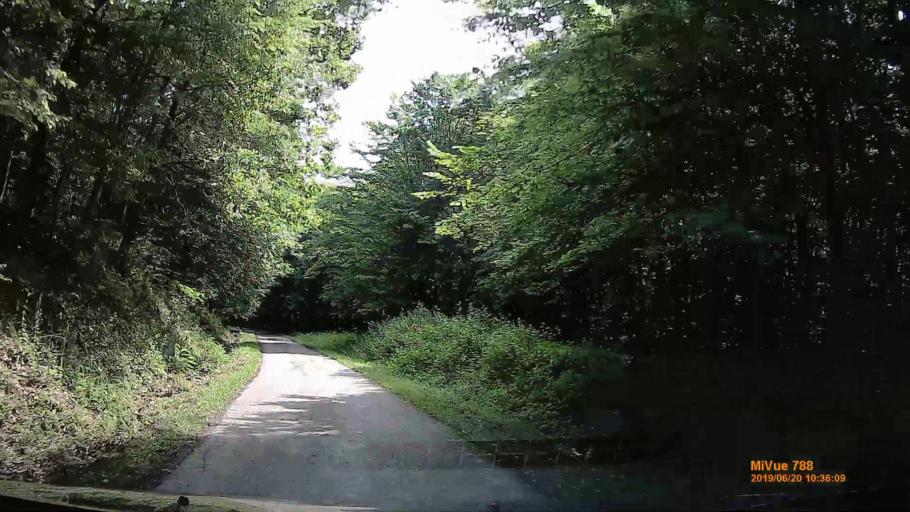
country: HU
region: Baranya
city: Mecseknadasd
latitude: 46.2020
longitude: 18.5290
